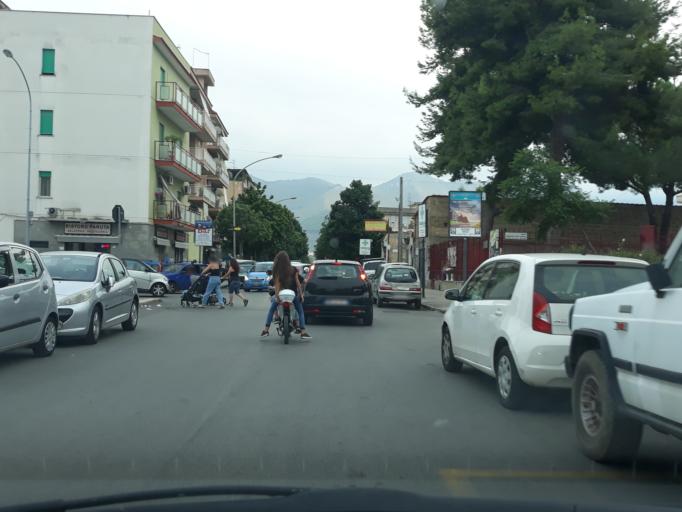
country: IT
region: Sicily
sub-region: Palermo
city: Monreale
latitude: 38.0965
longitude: 13.3186
